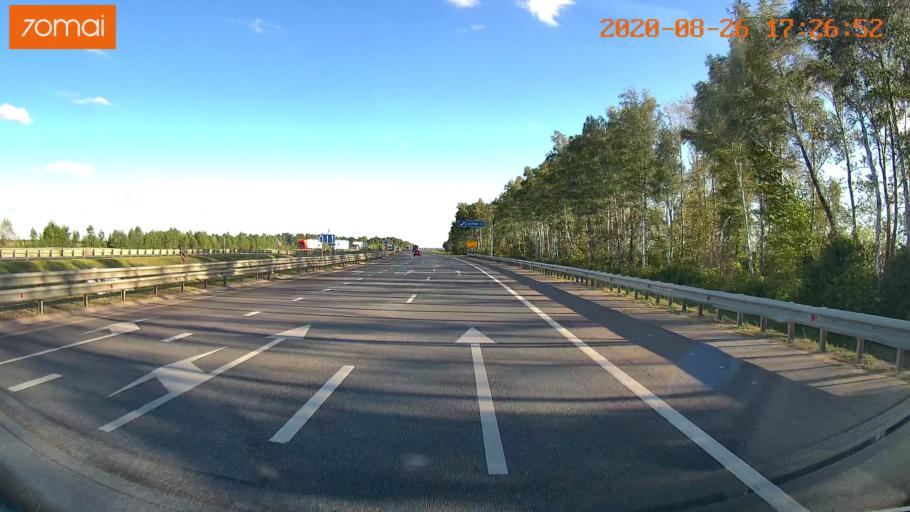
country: RU
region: Tula
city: Kazachka
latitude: 53.4807
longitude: 38.1201
